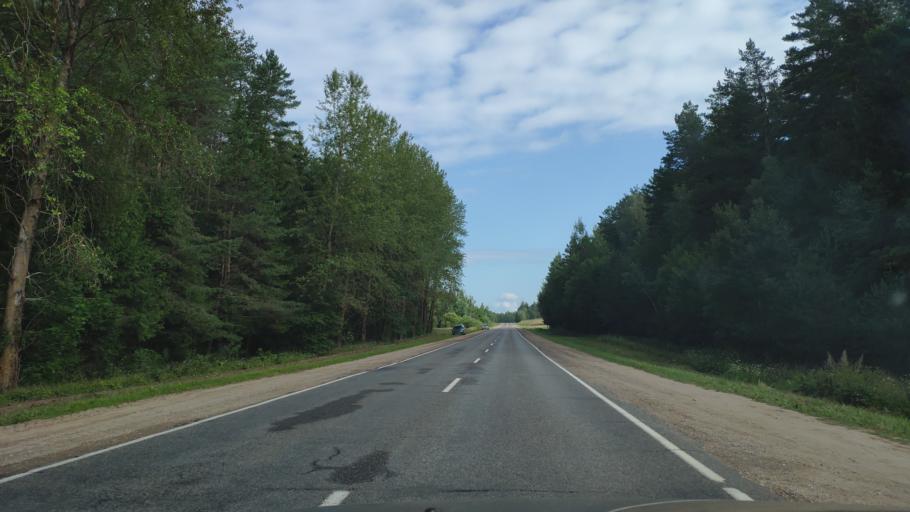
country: BY
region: Minsk
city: Zaslawye
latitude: 53.9573
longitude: 27.2454
